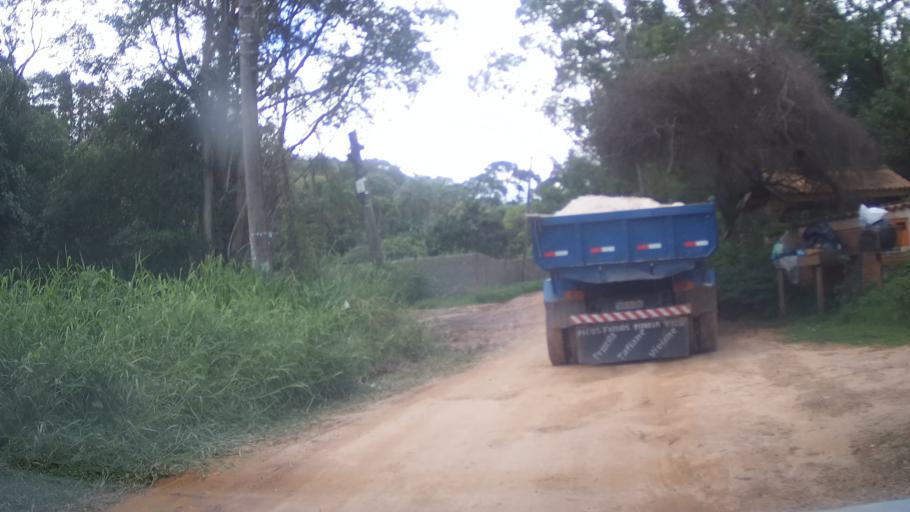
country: BR
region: Sao Paulo
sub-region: Campo Limpo Paulista
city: Campo Limpo Paulista
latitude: -23.2042
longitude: -46.7217
